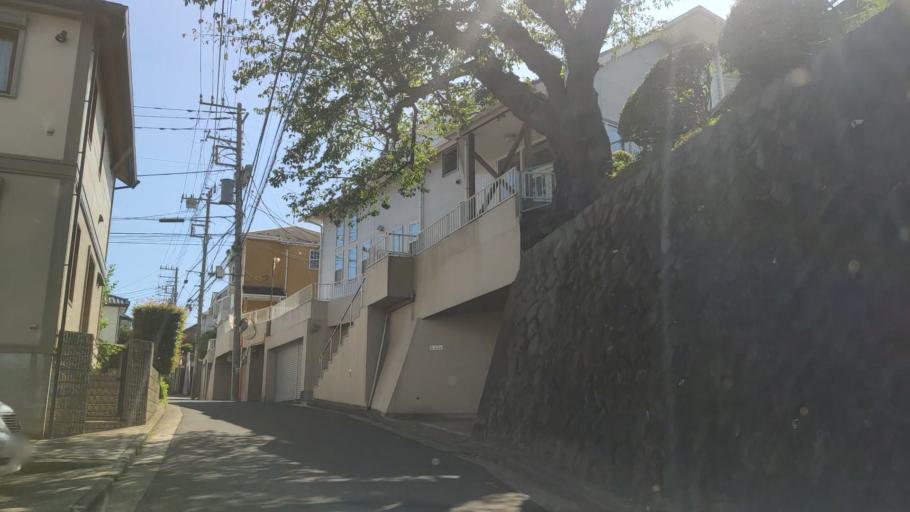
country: JP
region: Kanagawa
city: Yokohama
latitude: 35.5159
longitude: 139.6353
